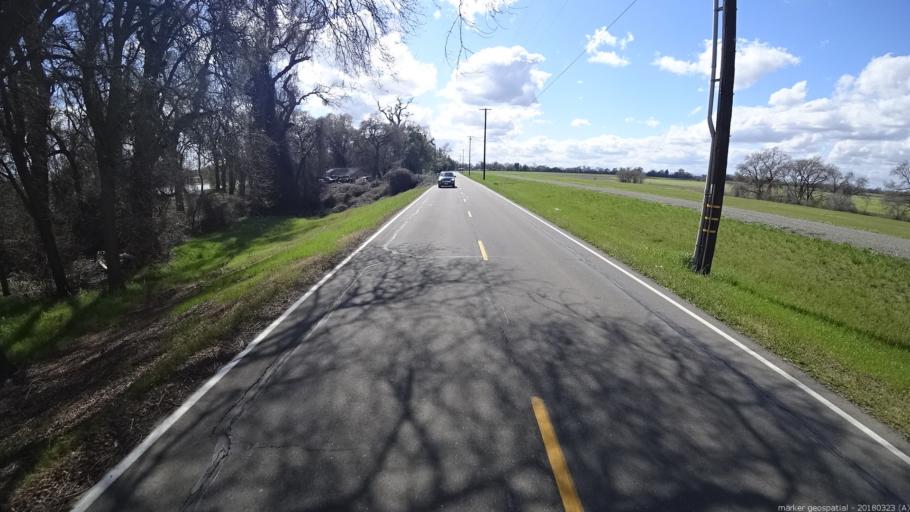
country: US
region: California
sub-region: Yolo County
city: West Sacramento
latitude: 38.6479
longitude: -121.5809
